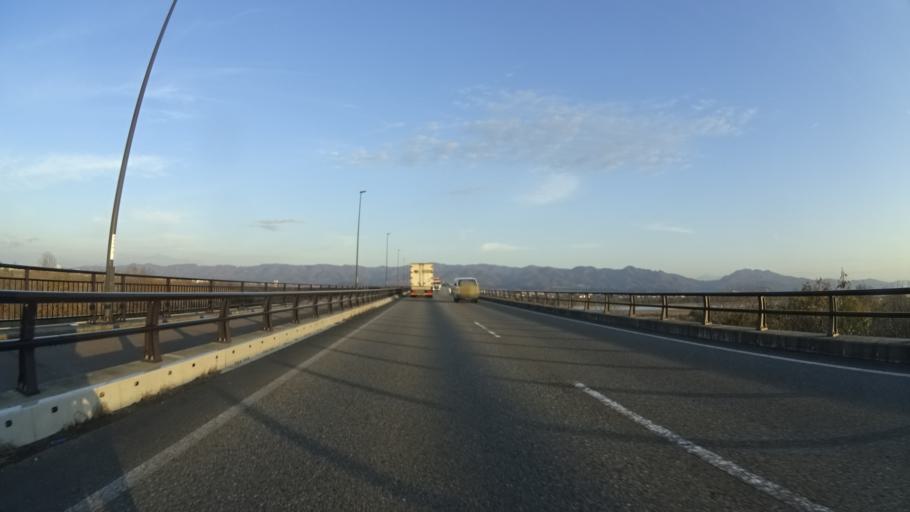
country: JP
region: Niigata
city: Nagaoka
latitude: 37.4320
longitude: 138.8172
